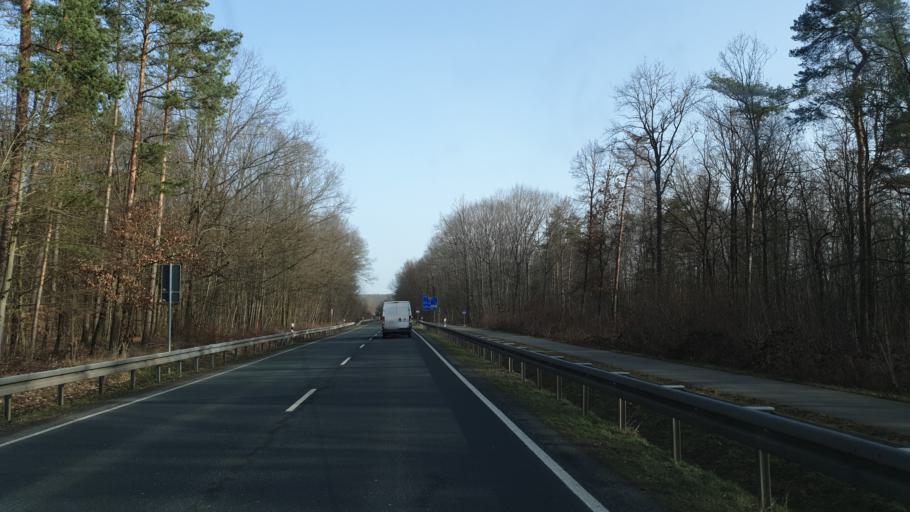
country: DE
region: Saxony
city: Naunhof
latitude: 51.2981
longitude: 12.5957
